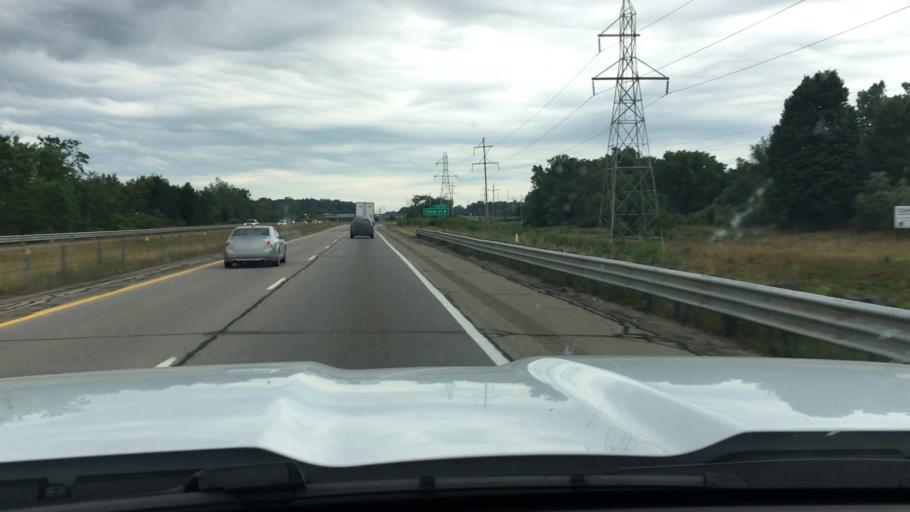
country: US
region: Michigan
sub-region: Kent County
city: Cutlerville
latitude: 42.7883
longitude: -85.6685
